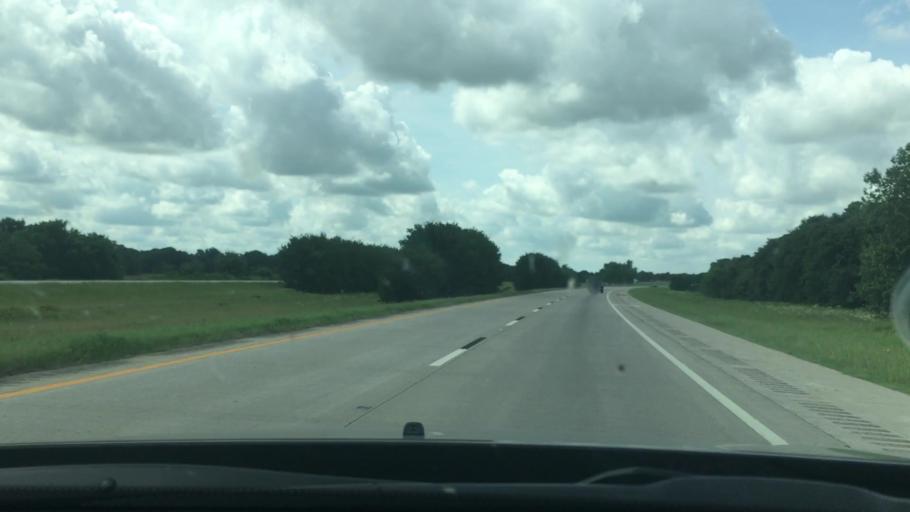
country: US
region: Oklahoma
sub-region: Love County
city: Marietta
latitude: 33.8289
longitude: -97.1305
